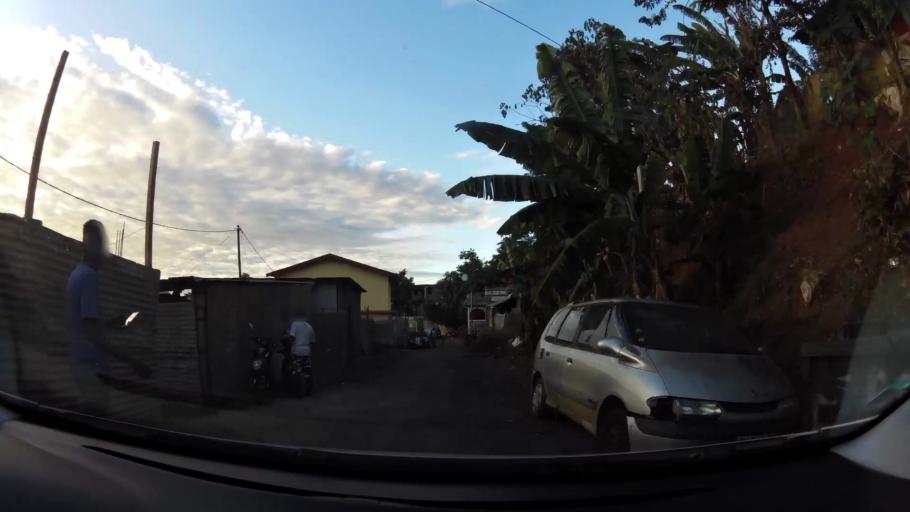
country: YT
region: Koungou
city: Koungou
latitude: -12.7347
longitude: 45.2000
